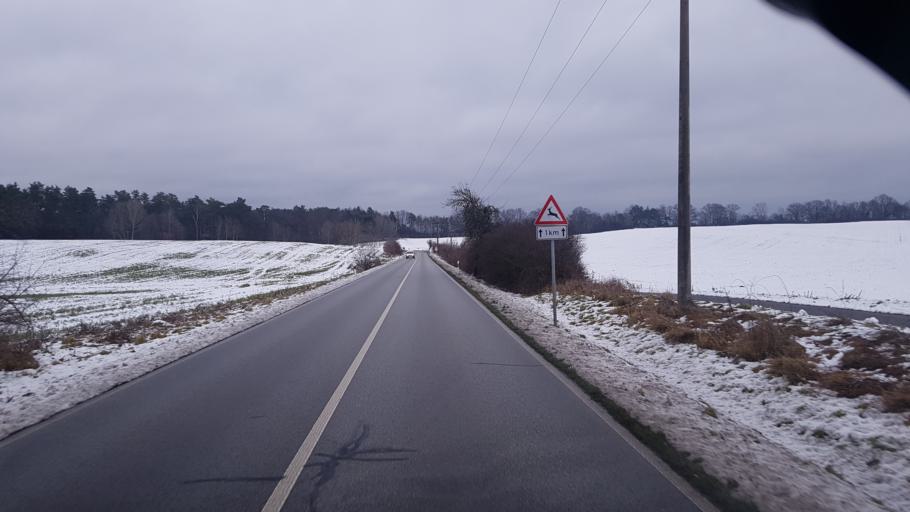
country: DE
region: Brandenburg
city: Eisenhuettenstadt
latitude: 52.1375
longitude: 14.6040
